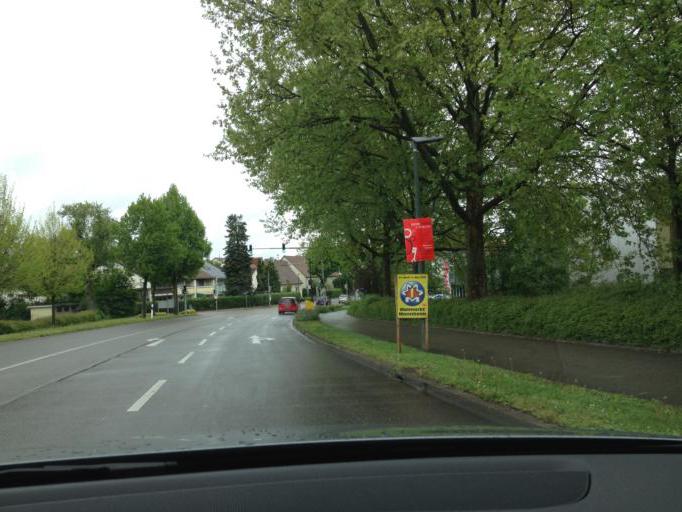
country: DE
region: Baden-Wuerttemberg
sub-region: Regierungsbezirk Stuttgart
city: Untereisesheim
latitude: 49.2063
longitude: 9.2032
